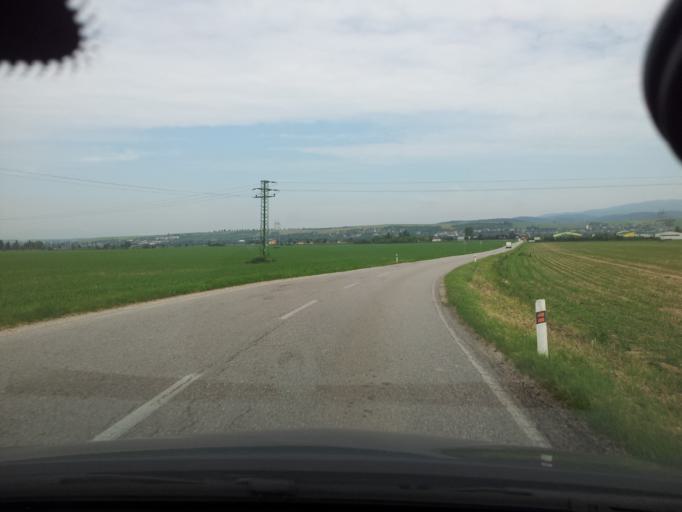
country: SK
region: Nitriansky
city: Partizanske
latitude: 48.6179
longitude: 18.4311
